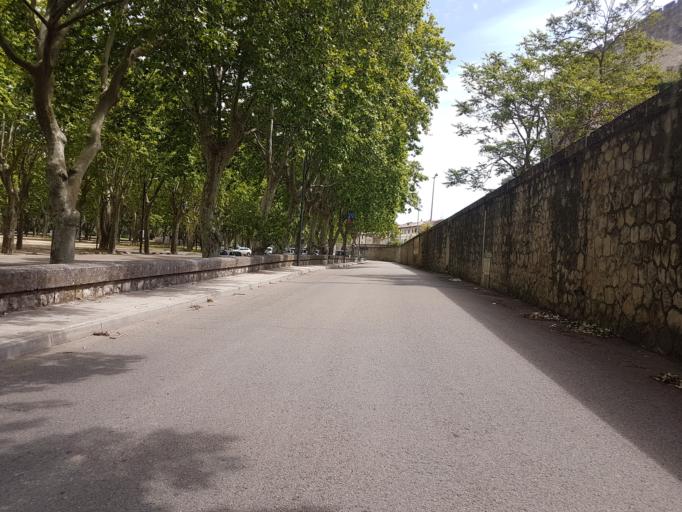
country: FR
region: Languedoc-Roussillon
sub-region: Departement du Gard
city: Beaucaire
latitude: 43.8112
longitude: 4.6446
